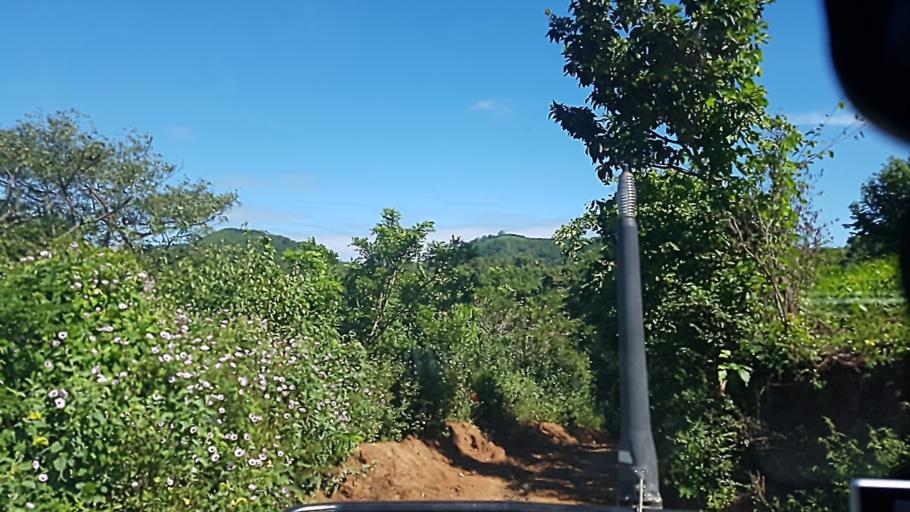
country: NI
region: Granada
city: Nandaime
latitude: 11.5663
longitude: -86.0880
